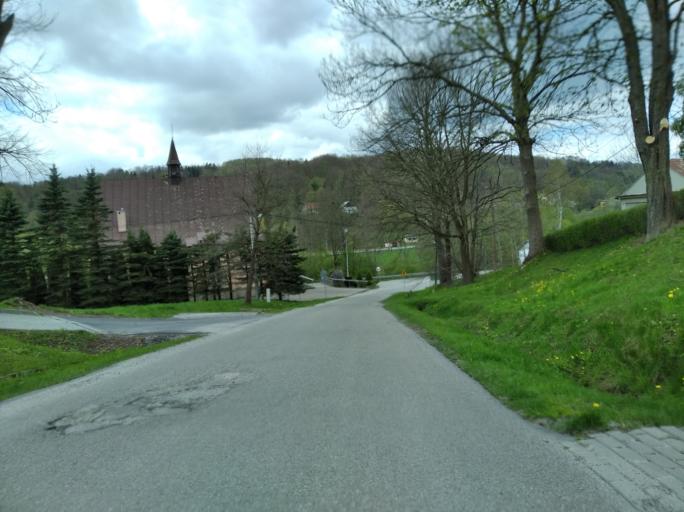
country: PL
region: Subcarpathian Voivodeship
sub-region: Powiat strzyzowski
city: Niebylec
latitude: 49.8780
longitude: 21.9072
